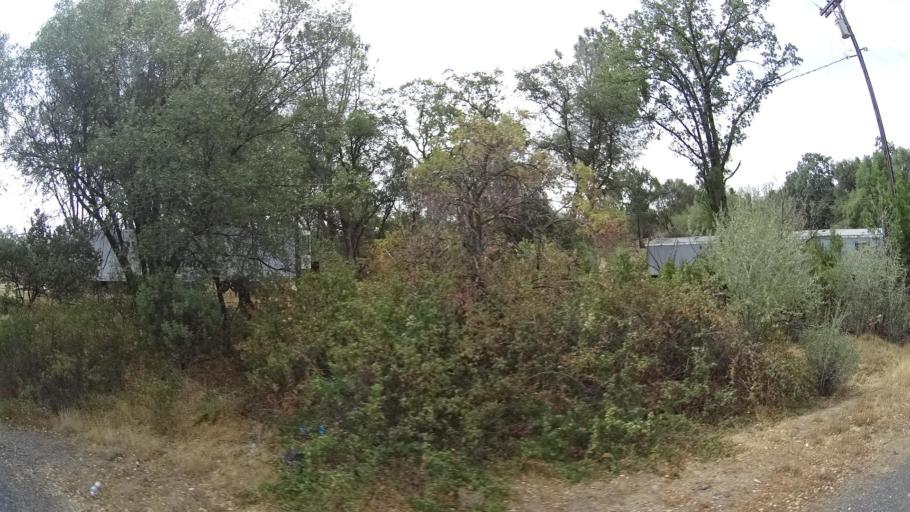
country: US
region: California
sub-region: Mariposa County
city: Midpines
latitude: 37.4758
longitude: -119.8713
